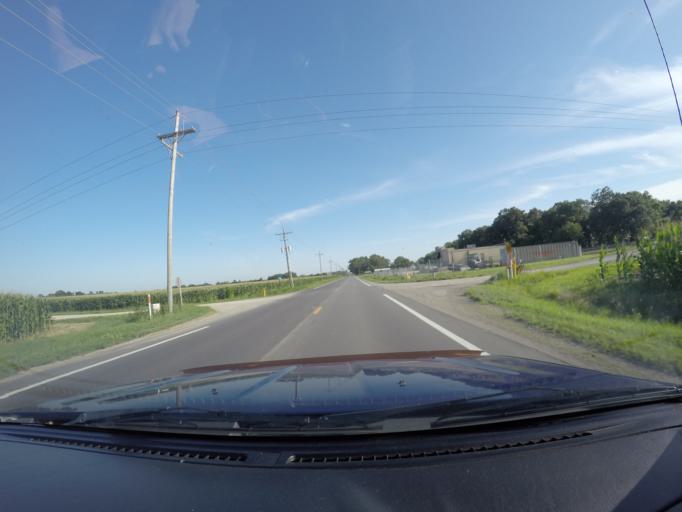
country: US
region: Kansas
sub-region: Douglas County
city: Lawrence
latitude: 39.0154
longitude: -95.2337
